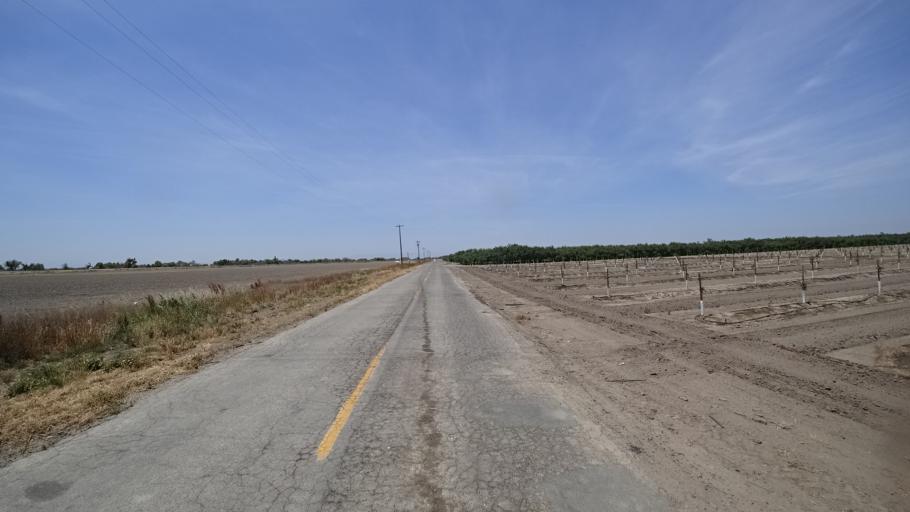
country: US
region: California
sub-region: Fresno County
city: Riverdale
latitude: 36.3875
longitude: -119.8906
